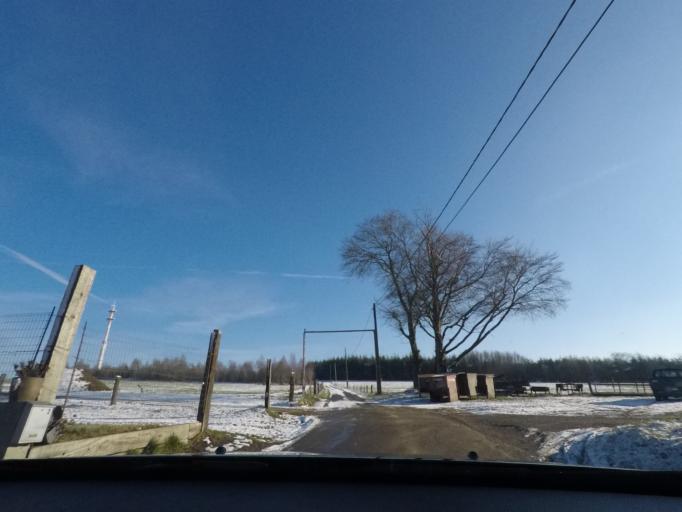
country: BE
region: Wallonia
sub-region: Province du Luxembourg
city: Neufchateau
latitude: 49.8329
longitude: 5.4657
